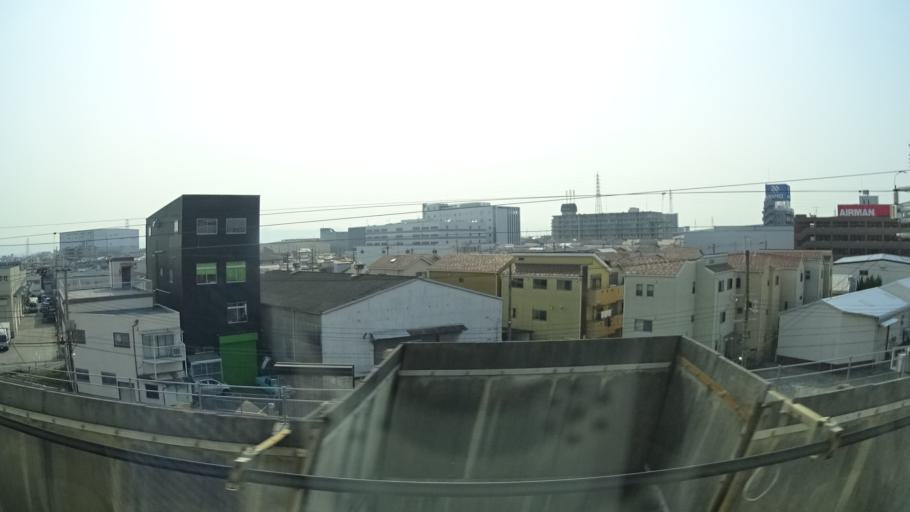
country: JP
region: Osaka
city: Kadoma
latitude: 34.7714
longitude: 135.5663
